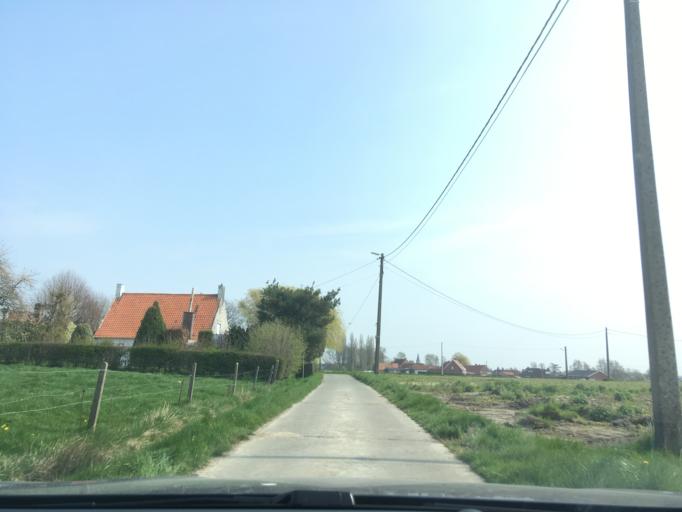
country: BE
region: Flanders
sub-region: Provincie West-Vlaanderen
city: Ardooie
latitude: 50.9808
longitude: 3.1824
